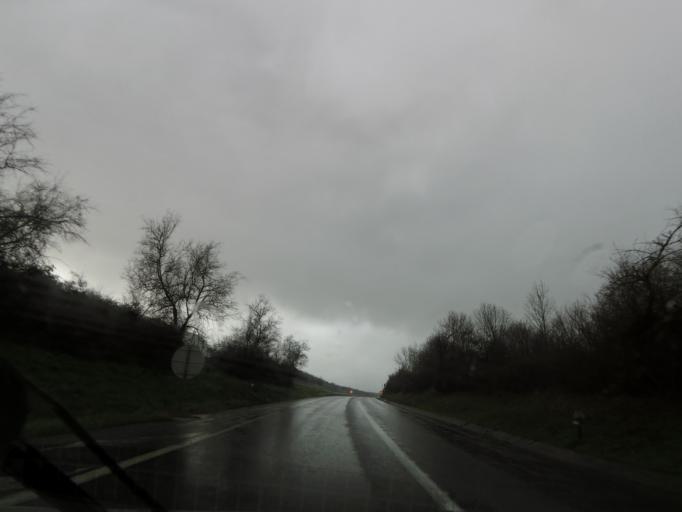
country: FR
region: Bourgogne
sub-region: Departement de Saone-et-Loire
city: Sance
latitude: 46.3511
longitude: 4.8279
